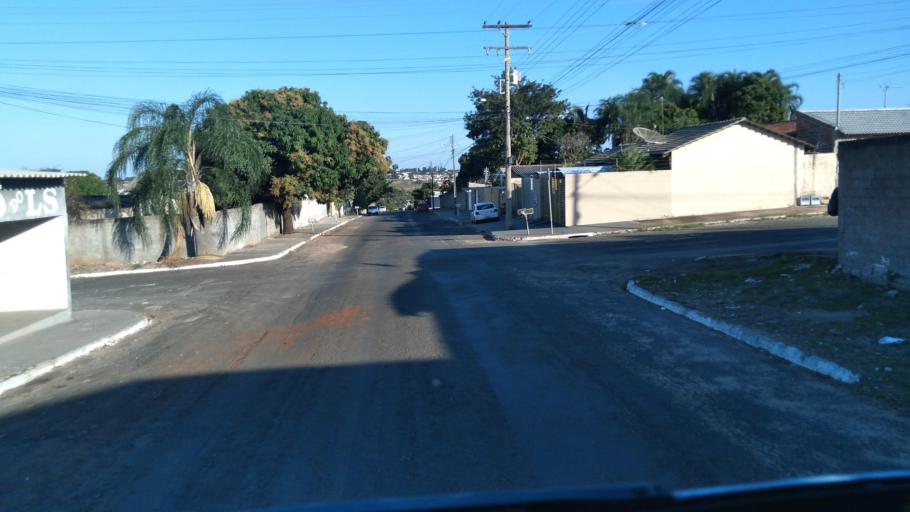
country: BR
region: Goias
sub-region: Mineiros
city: Mineiros
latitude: -17.5571
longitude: -52.5467
